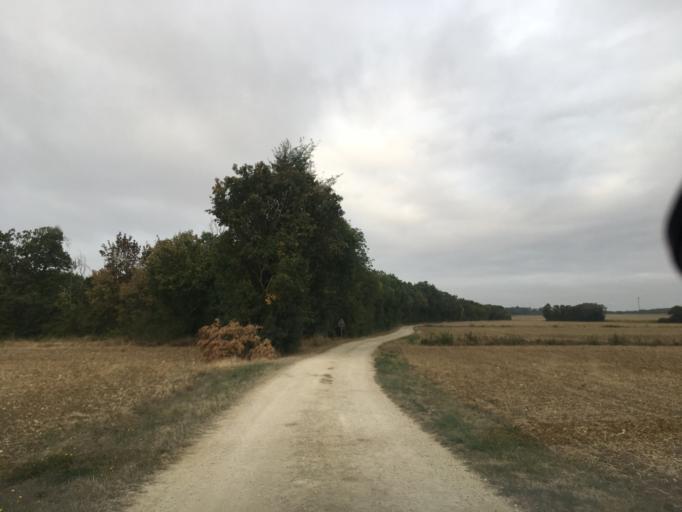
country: FR
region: Poitou-Charentes
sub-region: Departement des Deux-Sevres
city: Beauvoir-sur-Niort
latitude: 46.0886
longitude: -0.5162
